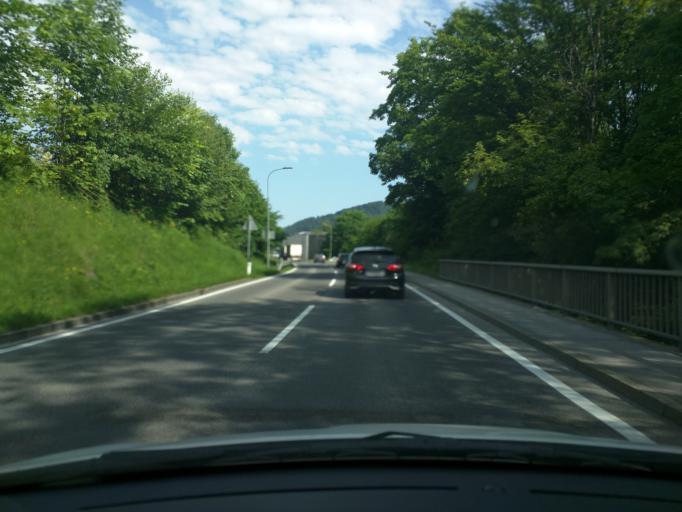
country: AT
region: Lower Austria
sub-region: Waidhofen an der Ybbs Stadt
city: Waidhofen an der Ybbs
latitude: 47.9734
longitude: 14.7576
